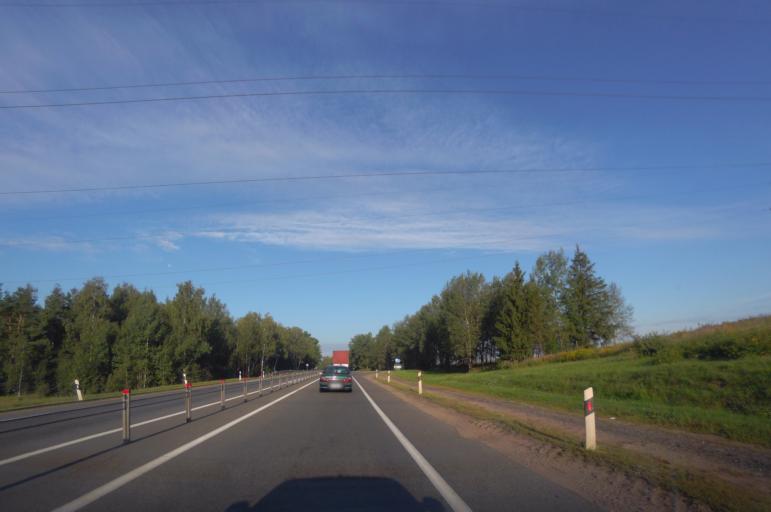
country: BY
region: Minsk
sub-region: Smalyavitski Rayon
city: Usjazh
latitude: 54.0299
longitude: 27.9860
